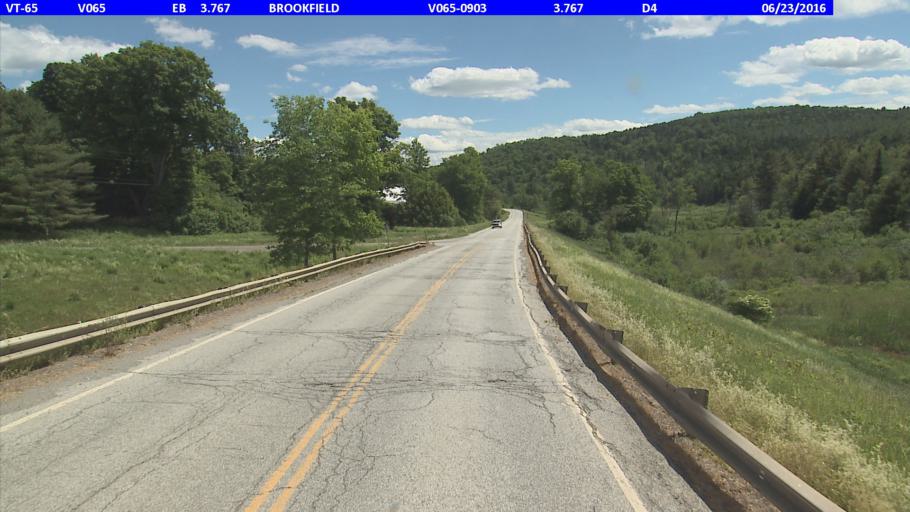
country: US
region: Vermont
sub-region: Orange County
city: Williamstown
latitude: 44.0361
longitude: -72.5925
